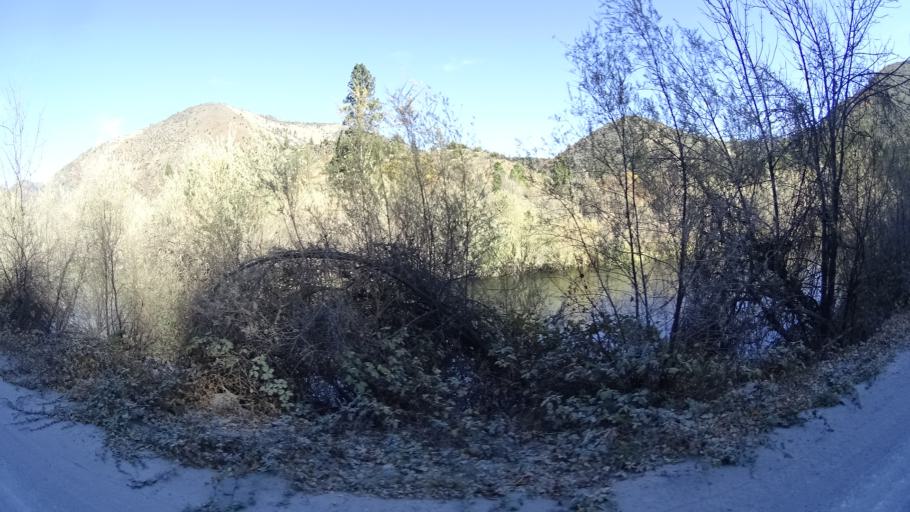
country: US
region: California
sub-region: Siskiyou County
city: Yreka
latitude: 41.8256
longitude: -122.6605
